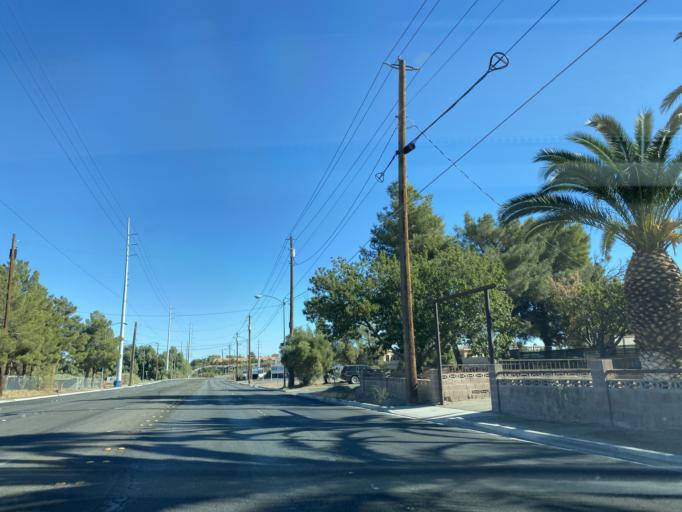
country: US
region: Nevada
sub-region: Clark County
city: Whitney
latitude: 36.0784
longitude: -115.0867
